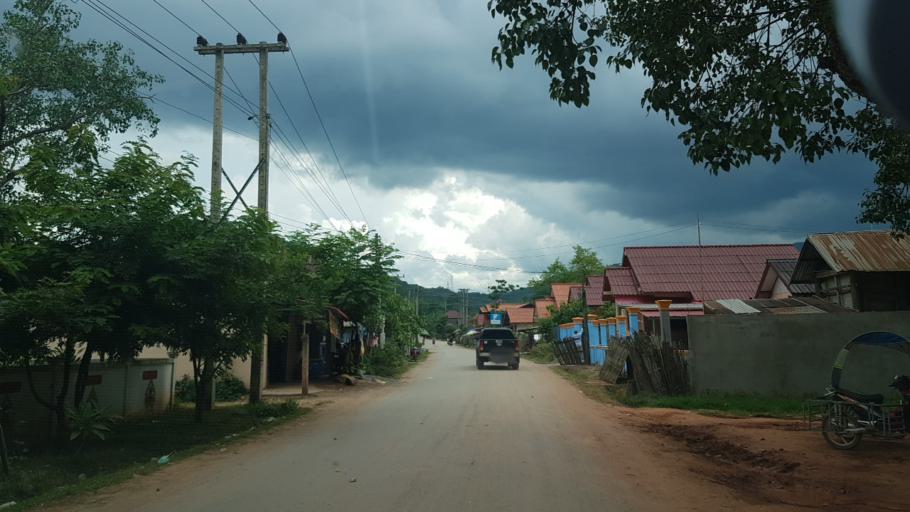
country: LA
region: Oudomxai
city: Muang Xay
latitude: 20.6738
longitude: 101.9681
